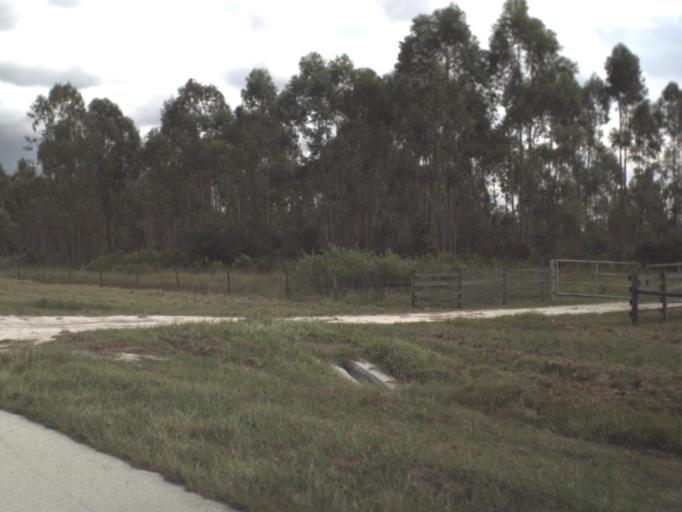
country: US
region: Florida
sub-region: Hendry County
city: Port LaBelle
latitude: 26.8751
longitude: -81.3587
